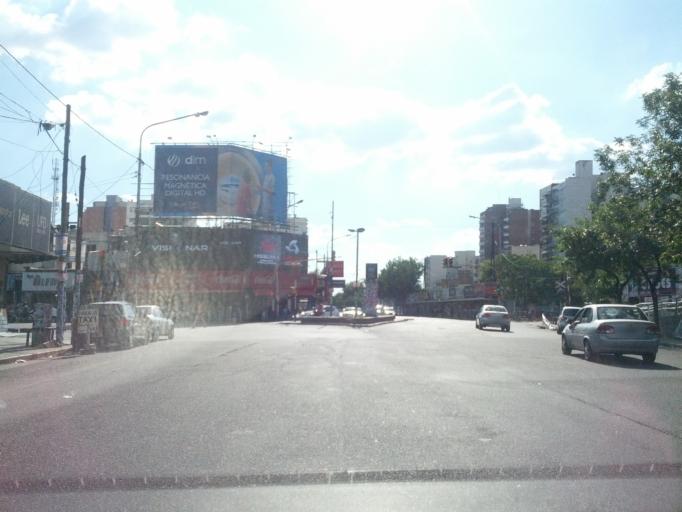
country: AR
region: Buenos Aires
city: San Justo
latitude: -34.6409
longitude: -58.5651
